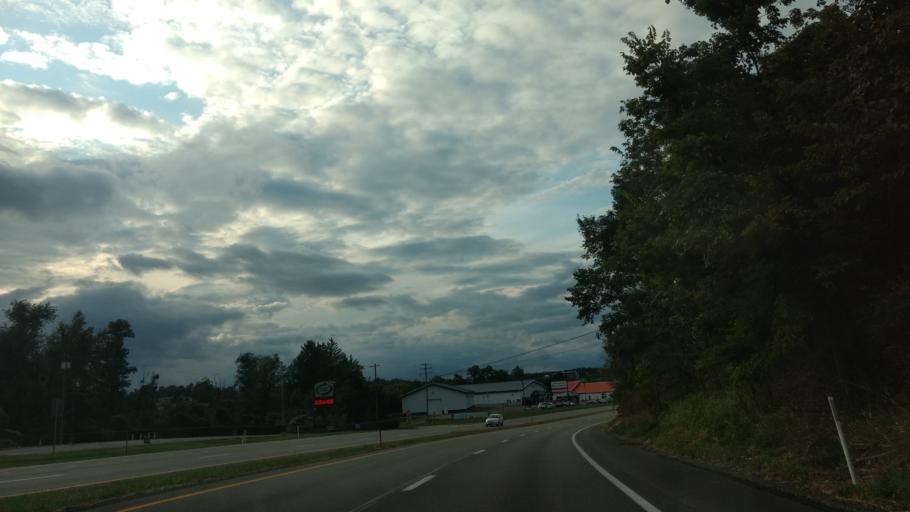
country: US
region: Pennsylvania
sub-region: Westmoreland County
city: Fellsburg
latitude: 40.1750
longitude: -79.8021
